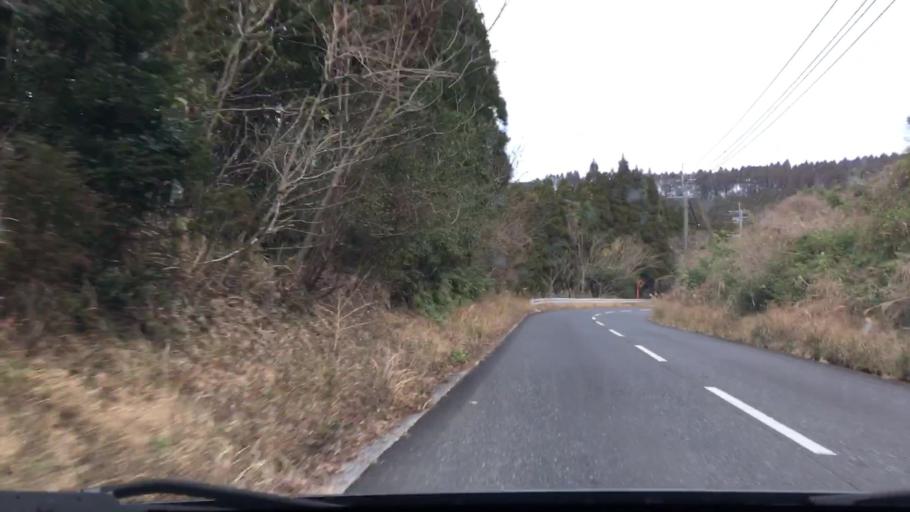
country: JP
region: Miyazaki
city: Nichinan
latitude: 31.6659
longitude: 131.3178
